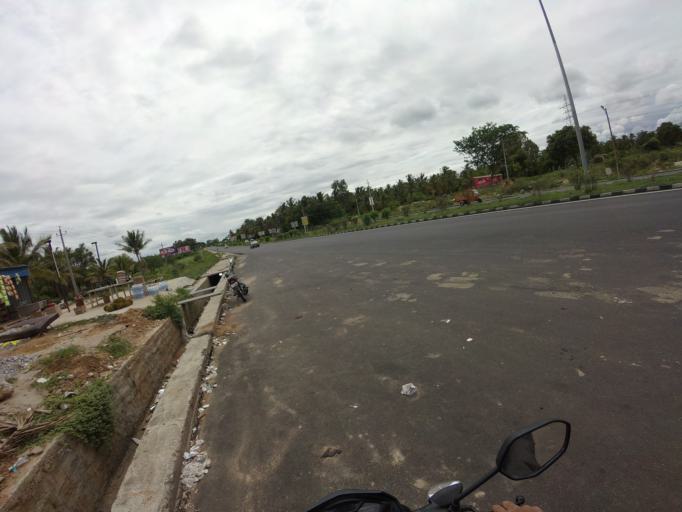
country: IN
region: Karnataka
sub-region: Mandya
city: Belluru
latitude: 12.9627
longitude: 76.7689
